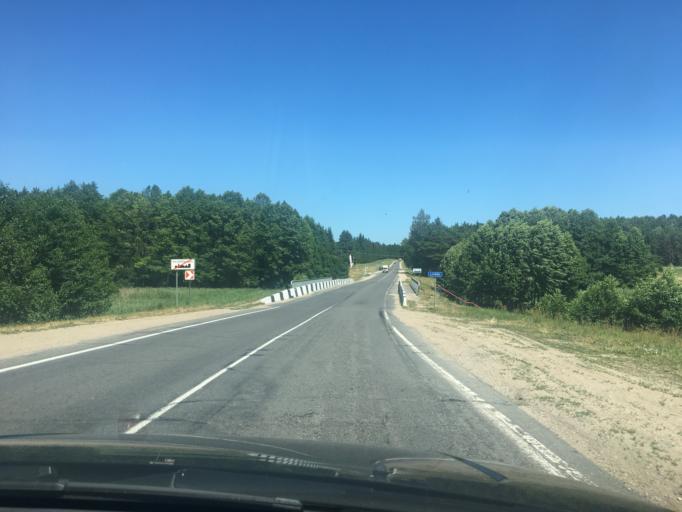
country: BY
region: Grodnenskaya
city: Hal'shany
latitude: 54.2141
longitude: 25.9660
